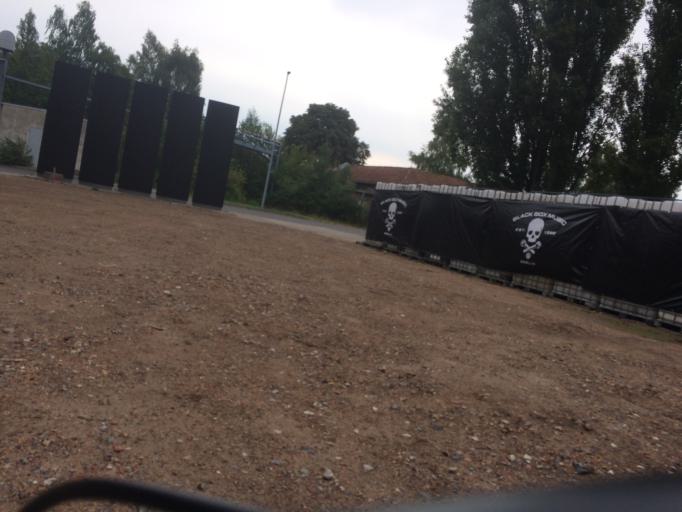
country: DE
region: Berlin
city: Markisches Viertel
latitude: 52.5903
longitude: 13.3576
